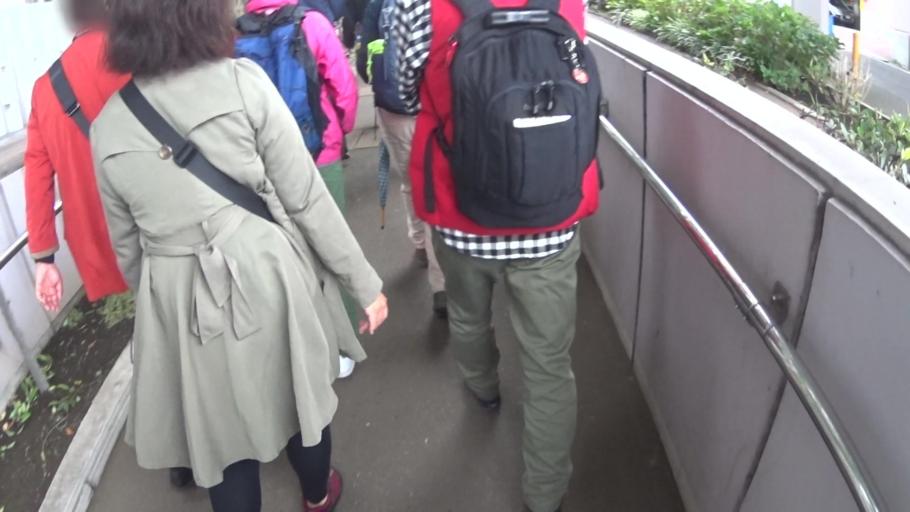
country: JP
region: Kanagawa
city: Hadano
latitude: 35.3774
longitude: 139.2279
